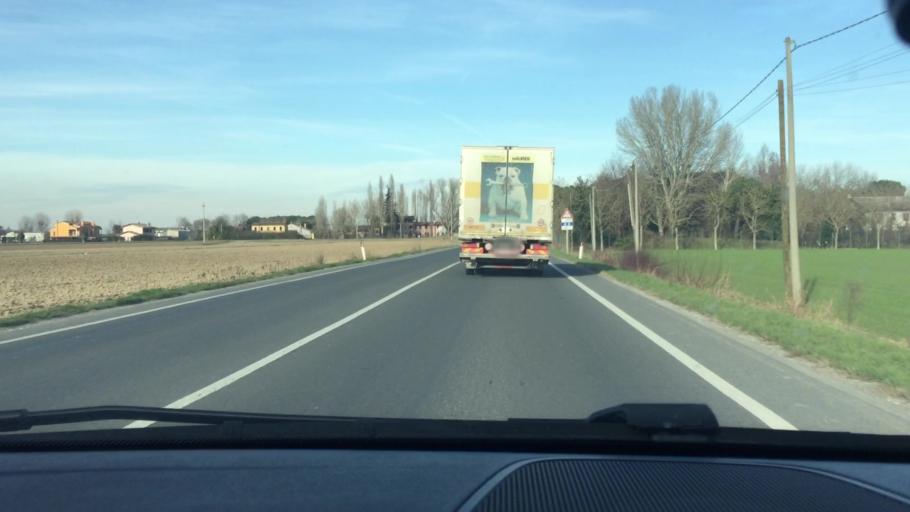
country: IT
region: Veneto
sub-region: Provincia di Padova
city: Codevigo
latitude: 45.2278
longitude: 12.1182
